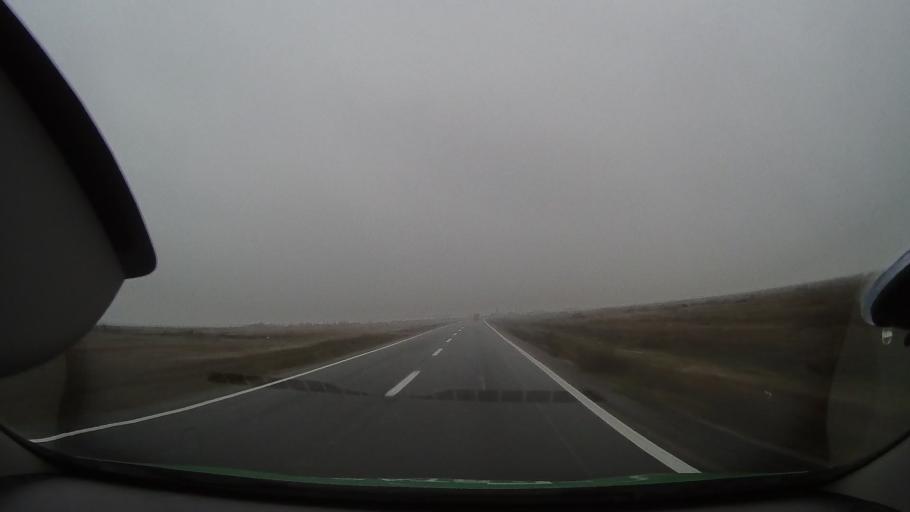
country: RO
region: Arad
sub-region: Comuna Craiova
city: Craiova
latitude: 46.6234
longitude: 21.9585
